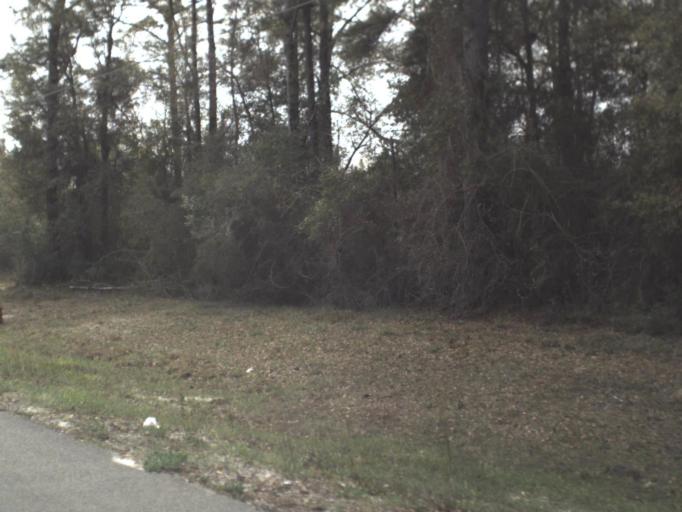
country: US
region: Florida
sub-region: Gulf County
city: Wewahitchka
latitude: 30.0524
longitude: -85.1880
